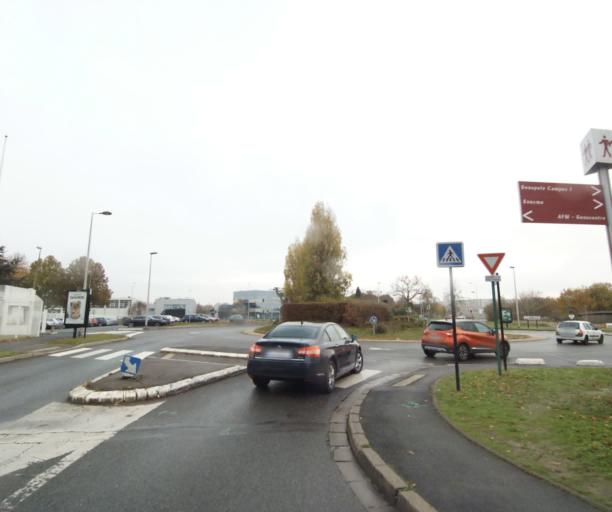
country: FR
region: Ile-de-France
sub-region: Departement de l'Essonne
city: Evry
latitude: 48.6197
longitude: 2.4495
